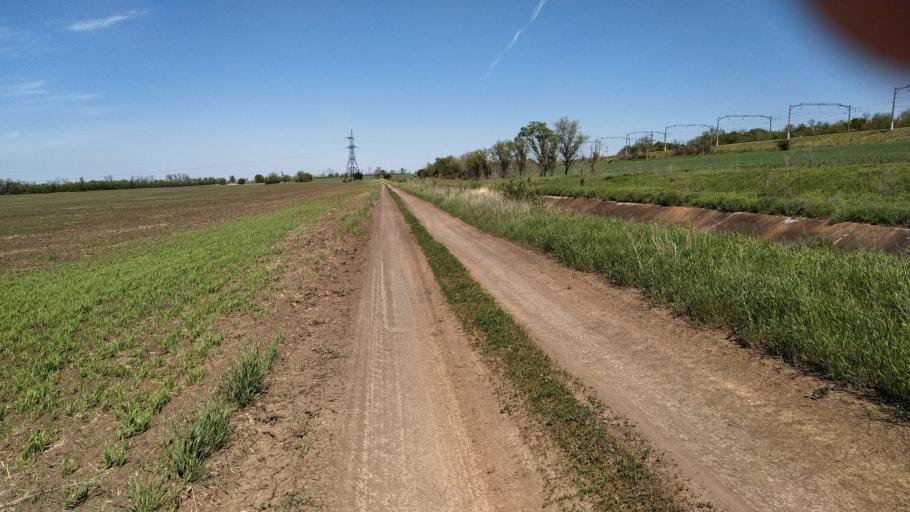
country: RU
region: Rostov
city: Kuleshovka
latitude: 47.0370
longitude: 39.6399
